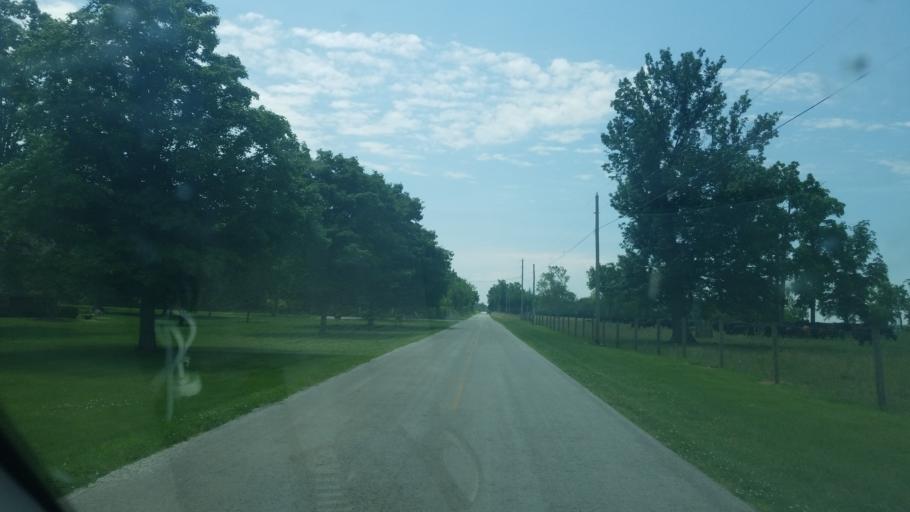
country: US
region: Ohio
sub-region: Wood County
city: North Baltimore
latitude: 41.2338
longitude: -83.6211
